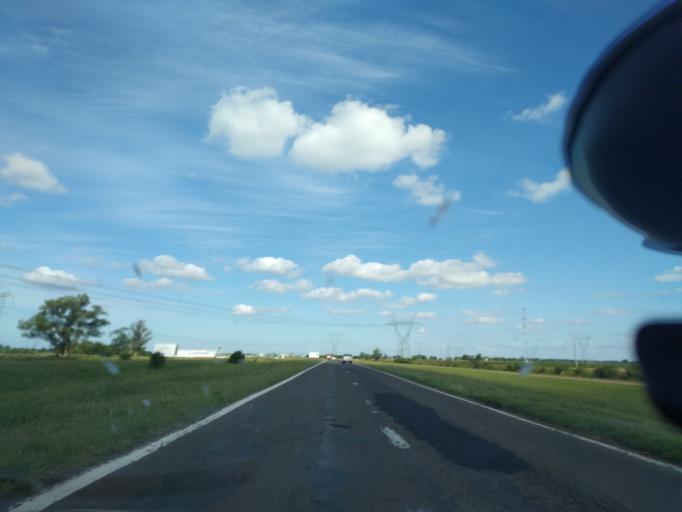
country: AR
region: Santa Fe
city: Roldan
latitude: -32.9225
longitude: -60.9180
